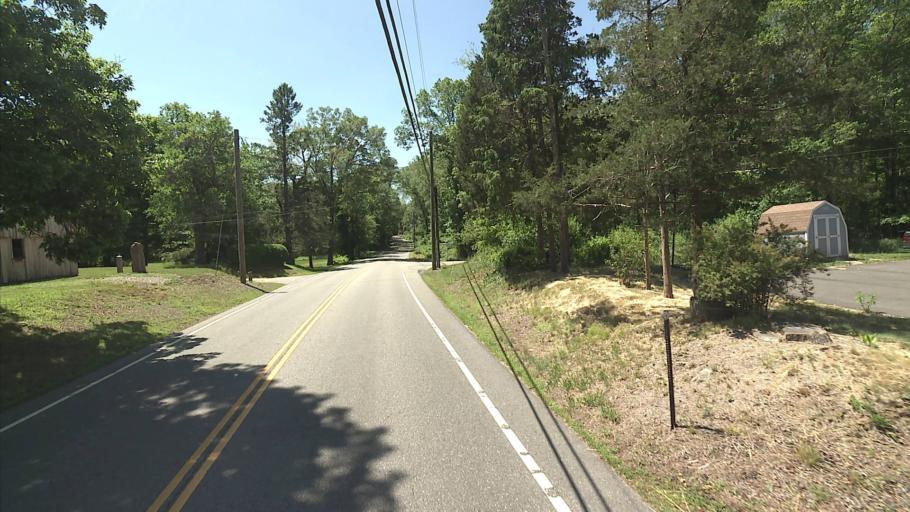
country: US
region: Rhode Island
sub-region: Washington County
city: Hopkinton
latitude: 41.4711
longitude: -71.8324
